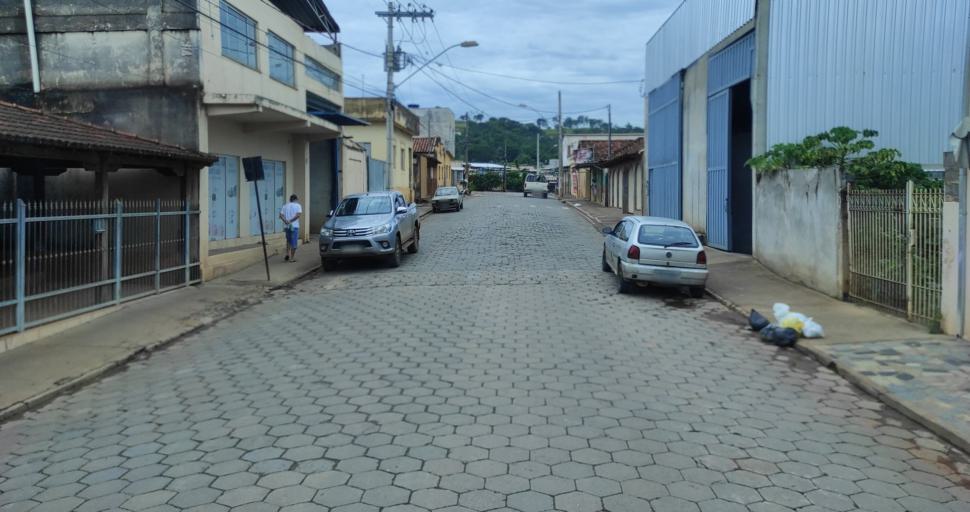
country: BR
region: Minas Gerais
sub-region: Arcos
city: Arcos
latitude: -20.3743
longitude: -45.6585
